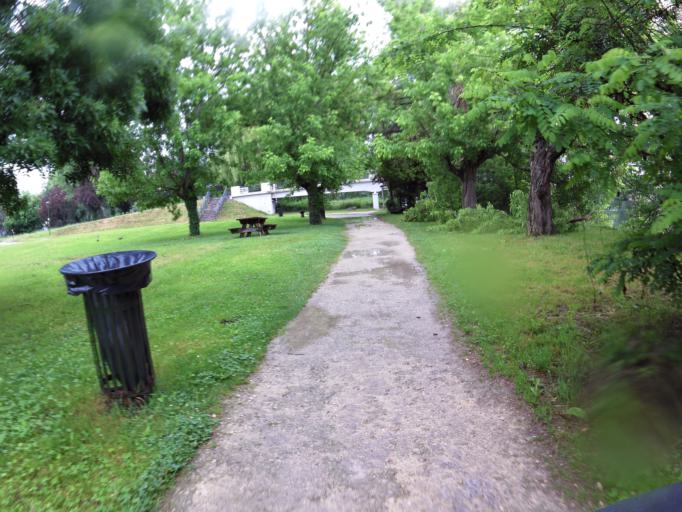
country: FR
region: Poitou-Charentes
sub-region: Departement de la Charente
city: Angouleme
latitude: 45.6587
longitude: 0.1591
